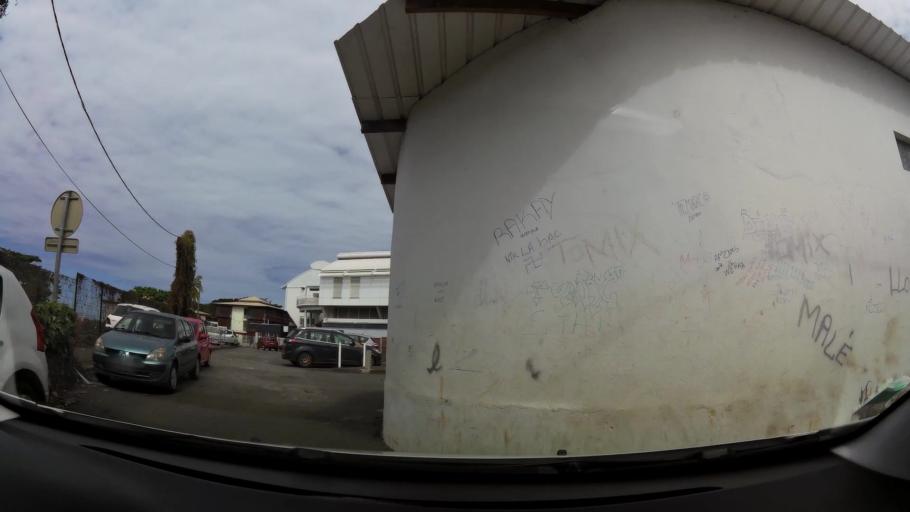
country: YT
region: Mamoudzou
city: Mamoudzou
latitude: -12.7772
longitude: 45.2278
